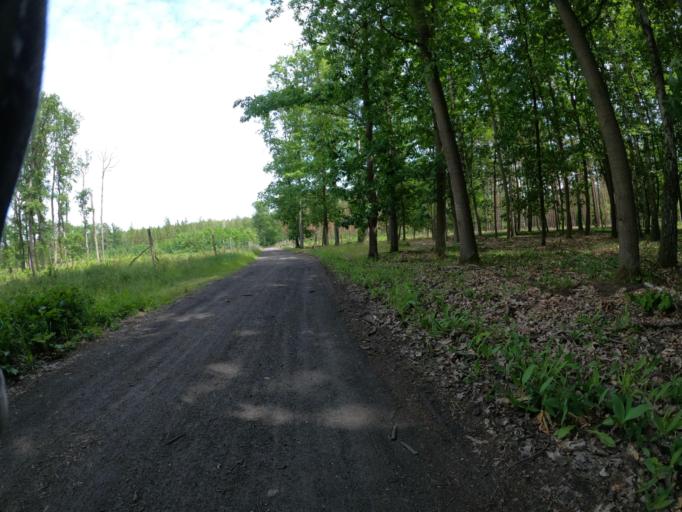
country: PL
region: West Pomeranian Voivodeship
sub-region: Powiat mysliborski
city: Boleszkowice
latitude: 52.6957
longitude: 14.5122
